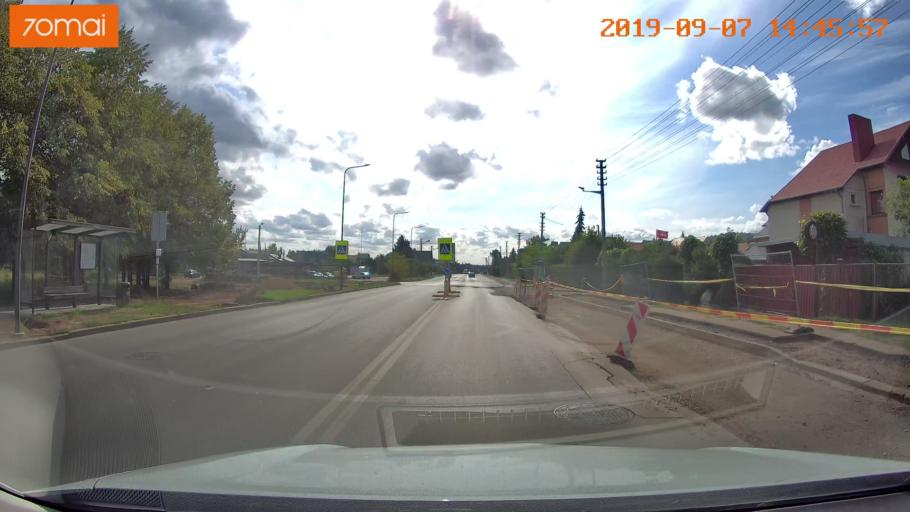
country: LT
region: Kauno apskritis
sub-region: Kaunas
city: Silainiai
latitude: 54.9293
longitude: 23.9074
